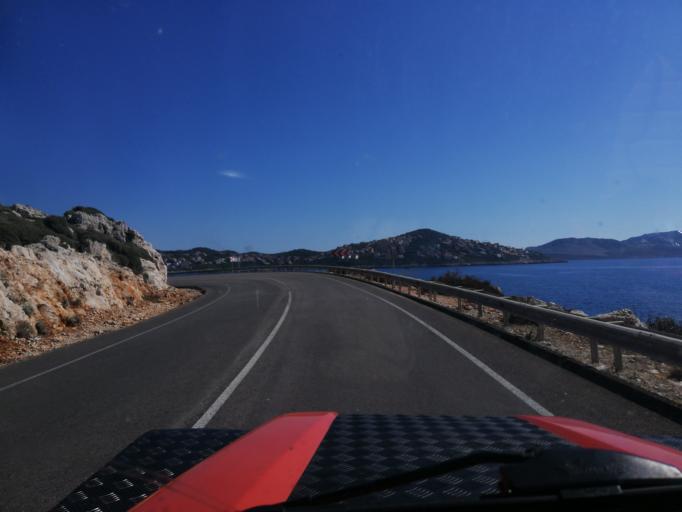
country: GR
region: South Aegean
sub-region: Nomos Dodekanisou
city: Megisti
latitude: 36.2024
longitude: 29.5796
